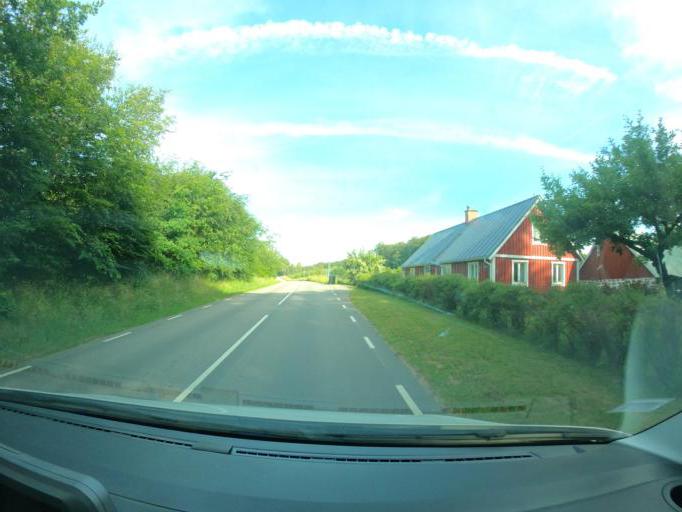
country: SE
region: Skane
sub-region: Bastads Kommun
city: Forslov
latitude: 56.3298
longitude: 12.9029
